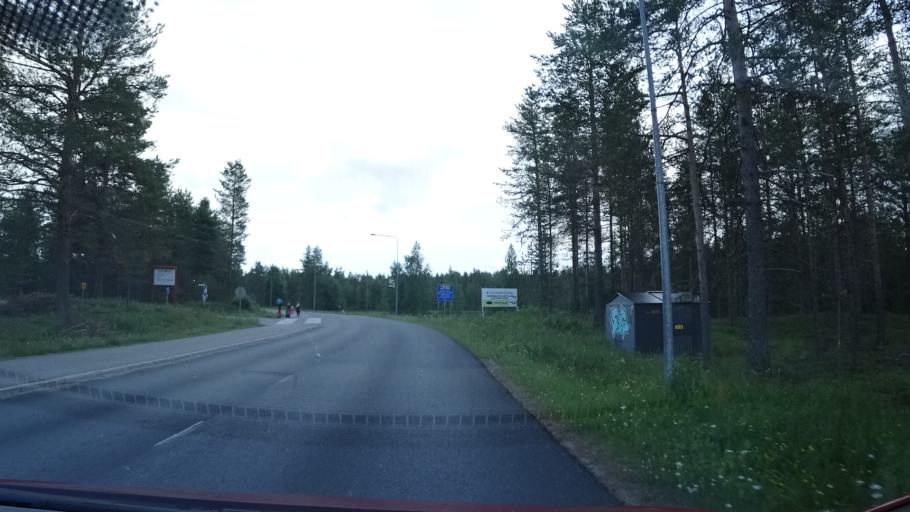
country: FI
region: Northern Ostrobothnia
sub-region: Koillismaa
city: Kuusamo
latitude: 65.9988
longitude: 29.1591
